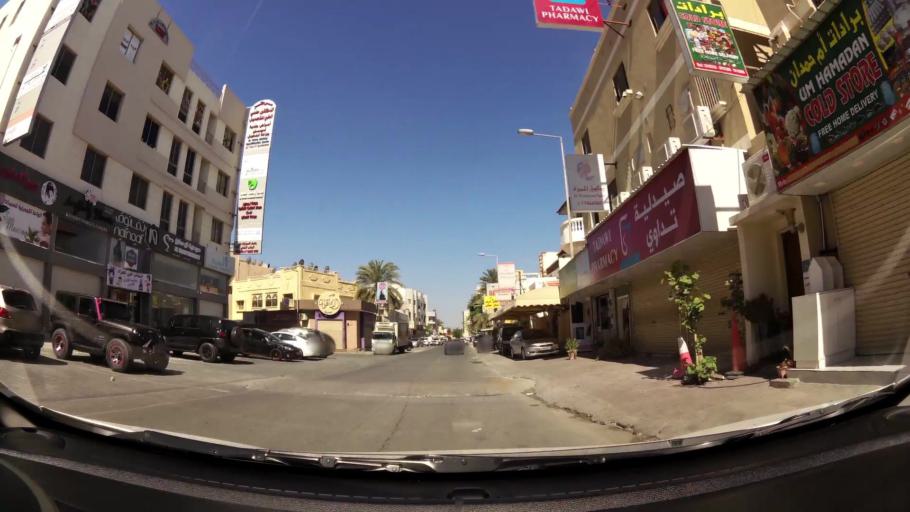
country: BH
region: Muharraq
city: Al Muharraq
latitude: 26.2616
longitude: 50.6183
